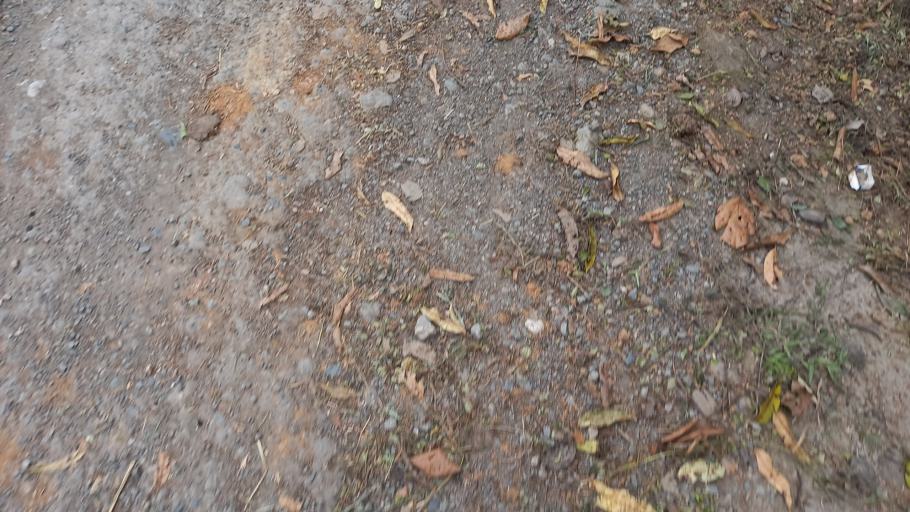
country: CO
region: Antioquia
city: Santa Barbara
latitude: 5.8372
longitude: -75.5741
